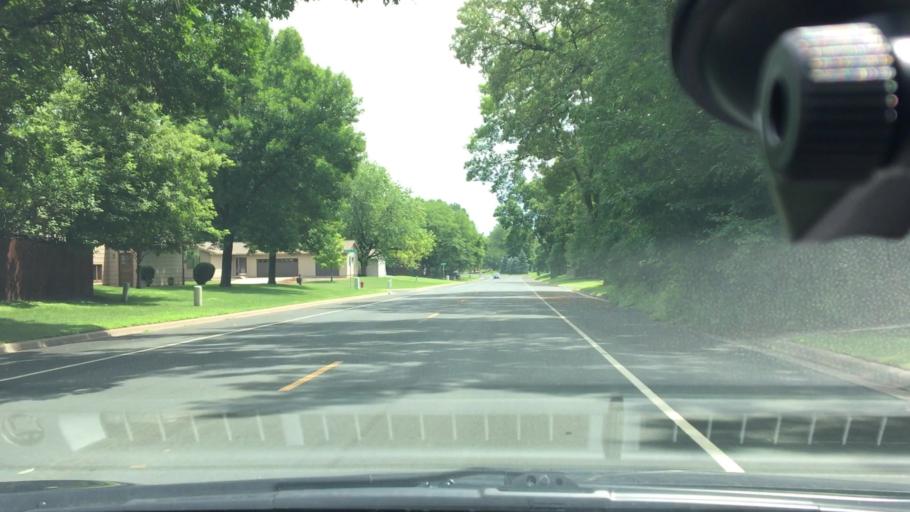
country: US
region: Minnesota
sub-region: Hennepin County
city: Maple Grove
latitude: 45.0674
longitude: -93.4377
